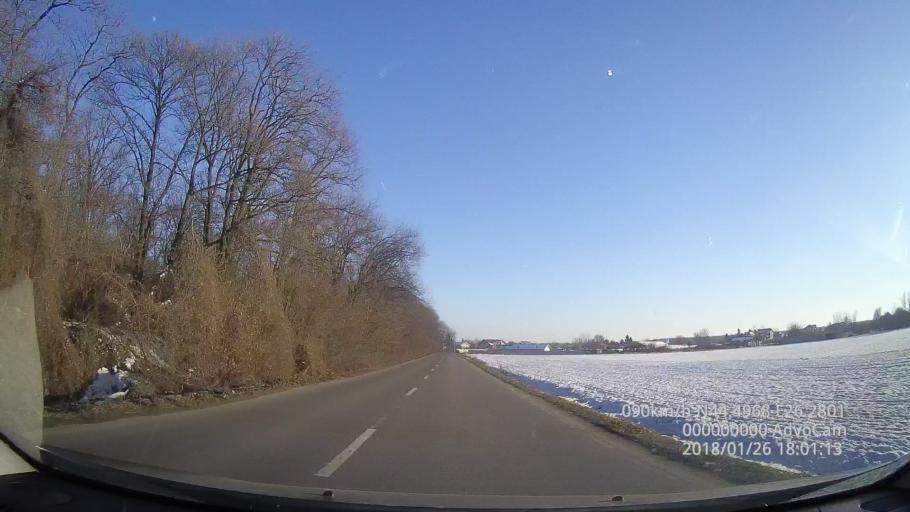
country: RO
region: Ilfov
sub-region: Comuna Ganeasa
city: Ganeasa
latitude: 44.4962
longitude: 26.2806
